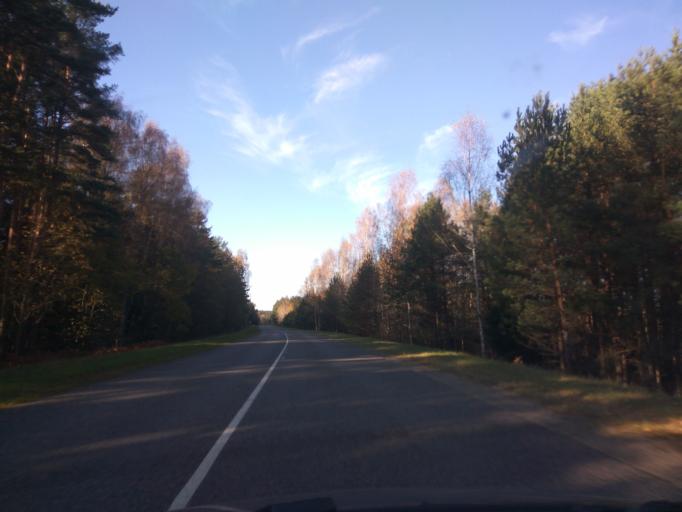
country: LV
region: Kuldigas Rajons
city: Kuldiga
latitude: 57.0686
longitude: 21.8051
